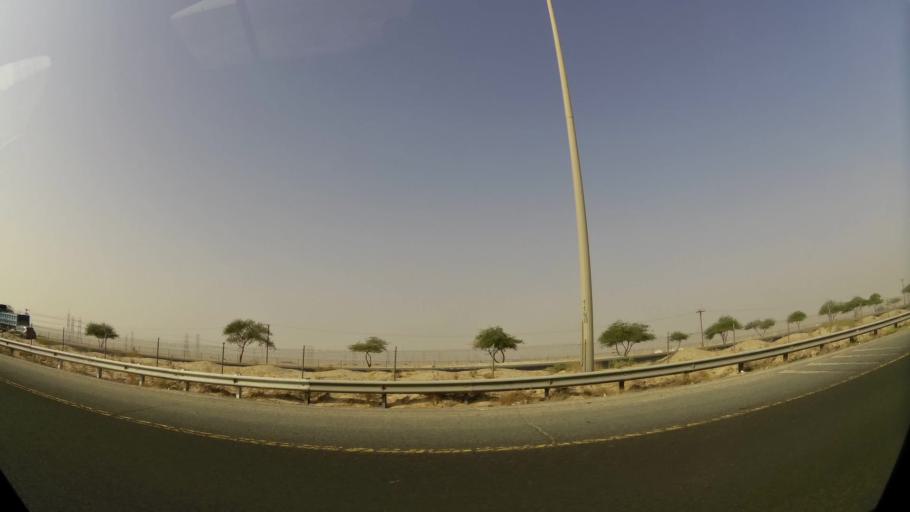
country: KW
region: Al Asimah
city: Ar Rabiyah
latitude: 29.1950
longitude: 47.8817
